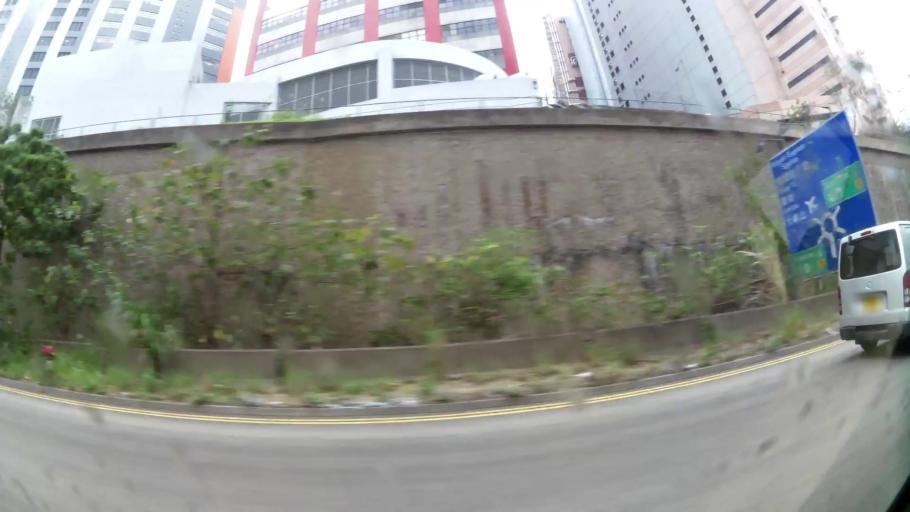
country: HK
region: Tsuen Wan
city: Tsuen Wan
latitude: 22.3634
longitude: 114.1192
